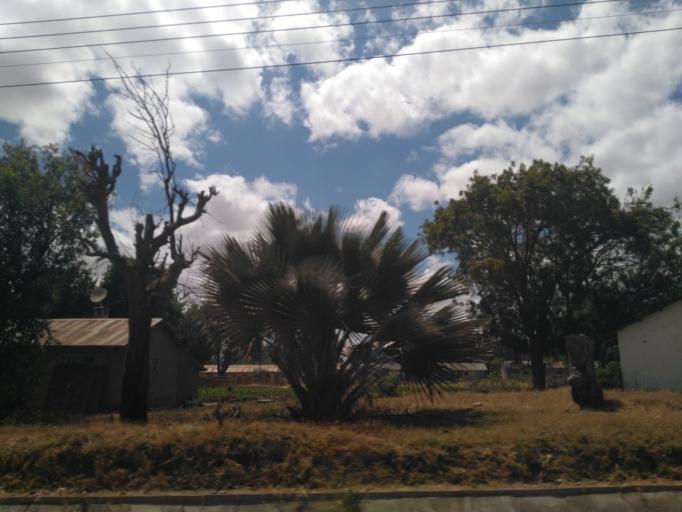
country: TZ
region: Dodoma
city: Dodoma
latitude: -6.1851
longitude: 35.7418
